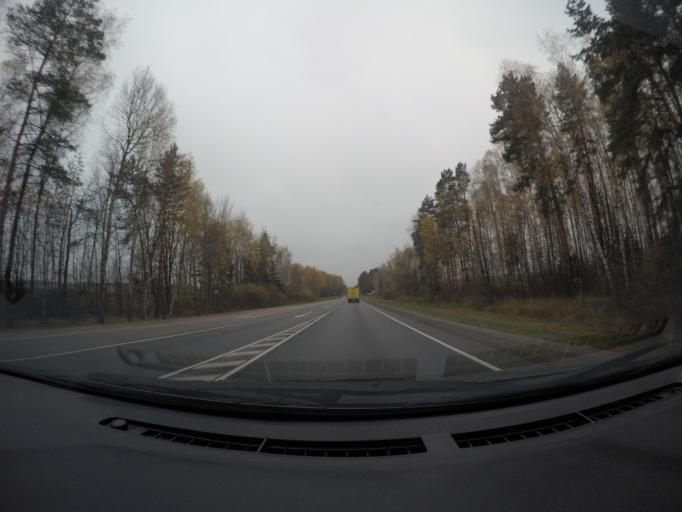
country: RU
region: Moskovskaya
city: Malyshevo
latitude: 55.5253
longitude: 38.3959
